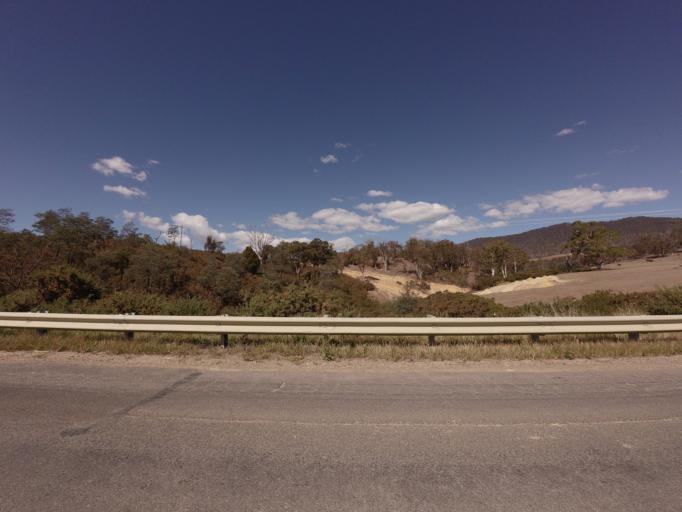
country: AU
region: Tasmania
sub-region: Break O'Day
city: St Helens
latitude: -41.6486
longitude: 147.9350
